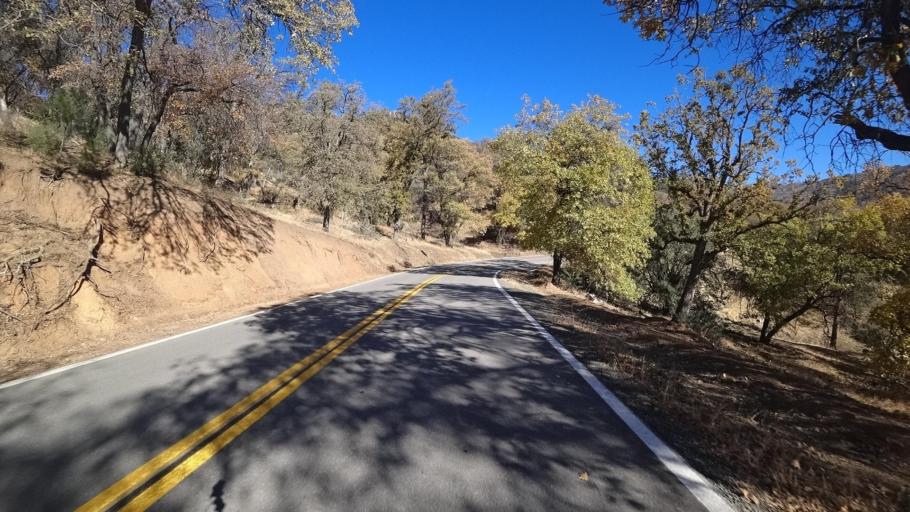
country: US
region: California
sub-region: Kern County
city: Alta Sierra
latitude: 35.7443
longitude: -118.5987
